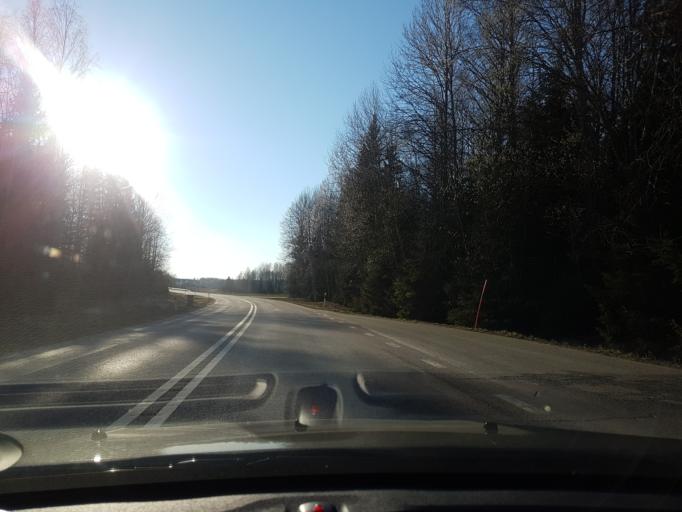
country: SE
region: Uppsala
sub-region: Heby Kommun
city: Morgongava
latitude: 59.9181
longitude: 17.0187
